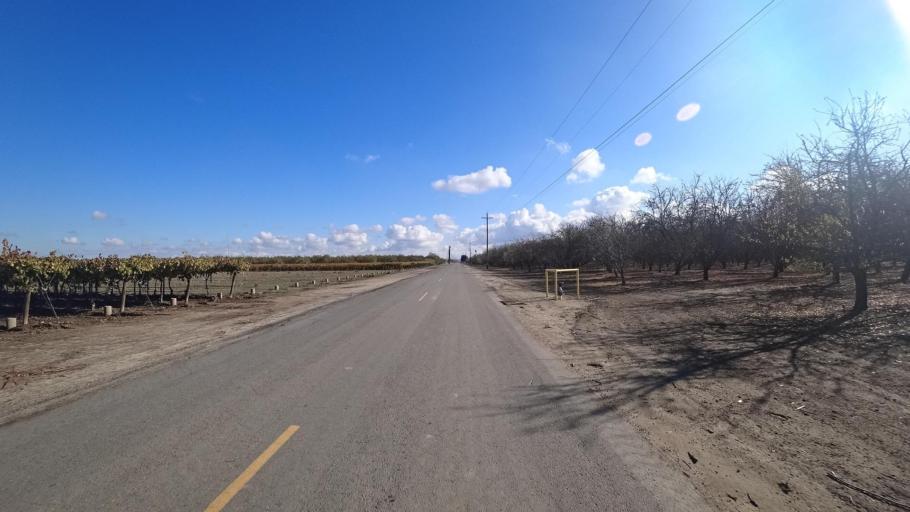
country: US
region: California
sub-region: Kern County
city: McFarland
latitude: 35.6598
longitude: -119.2455
